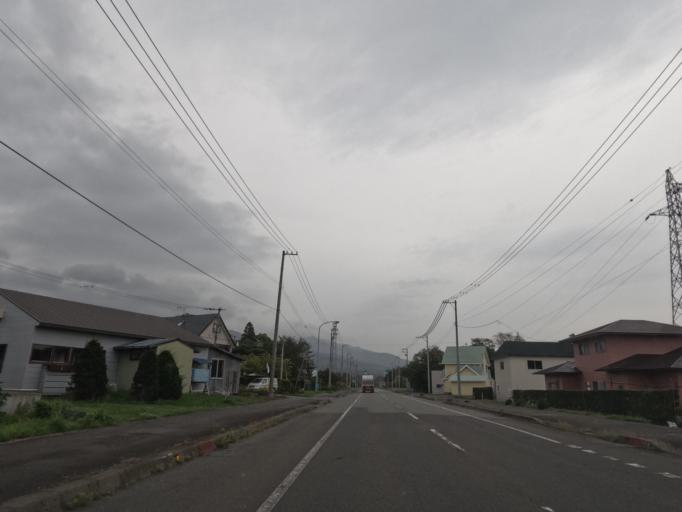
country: JP
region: Hokkaido
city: Date
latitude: 42.4848
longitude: 140.8777
